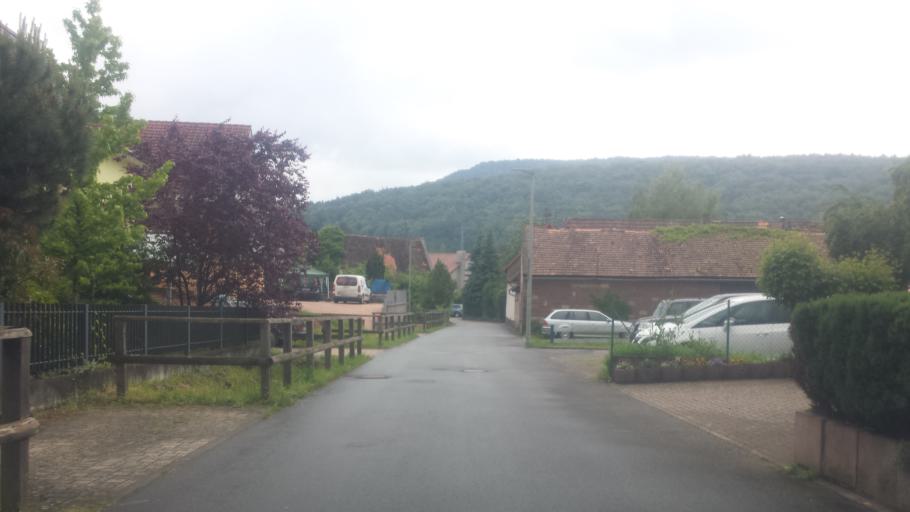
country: DE
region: Rheinland-Pfalz
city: Waldhambach
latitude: 49.1671
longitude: 7.9883
